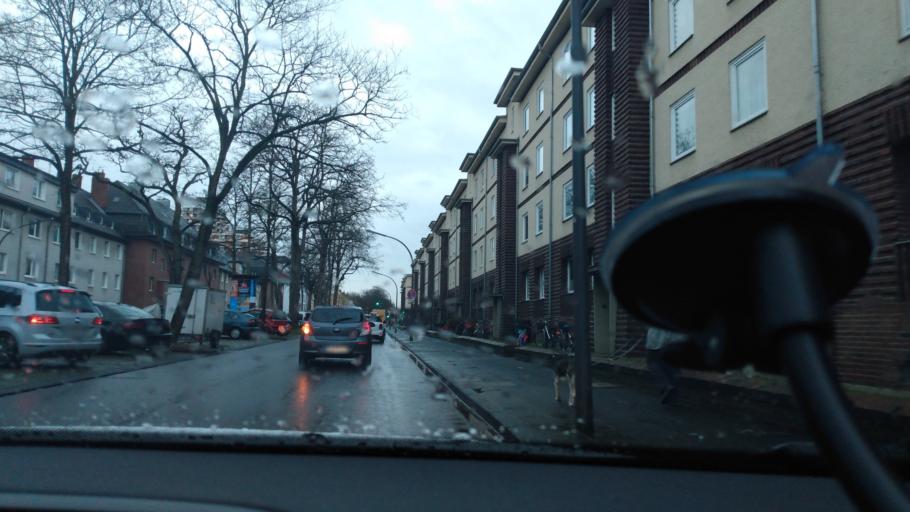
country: DE
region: North Rhine-Westphalia
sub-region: Regierungsbezirk Koln
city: Neustadt/Sued
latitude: 50.9071
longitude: 6.9454
